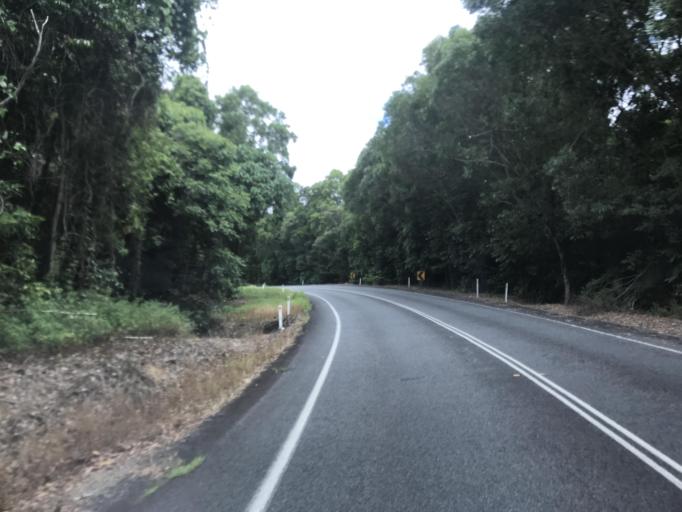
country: AU
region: Queensland
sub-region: Cassowary Coast
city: Innisfail
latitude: -17.8534
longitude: 146.0662
